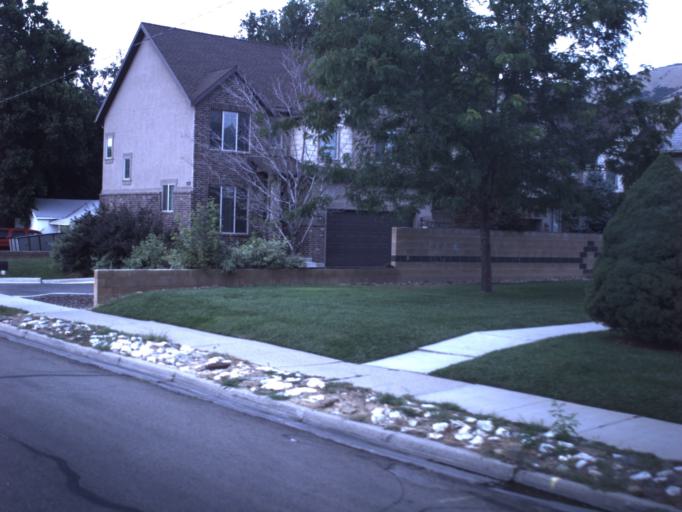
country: US
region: Utah
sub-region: Davis County
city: Bountiful
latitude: 40.8955
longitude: -111.8790
